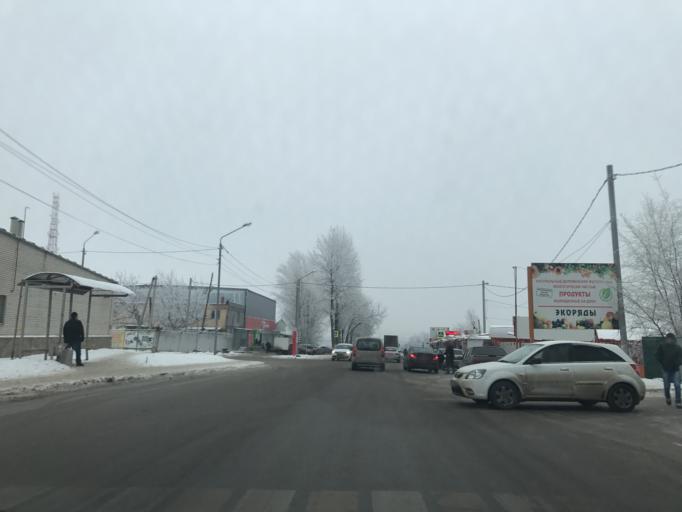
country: RU
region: Rostov
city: Aksay
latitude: 47.2422
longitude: 39.8344
